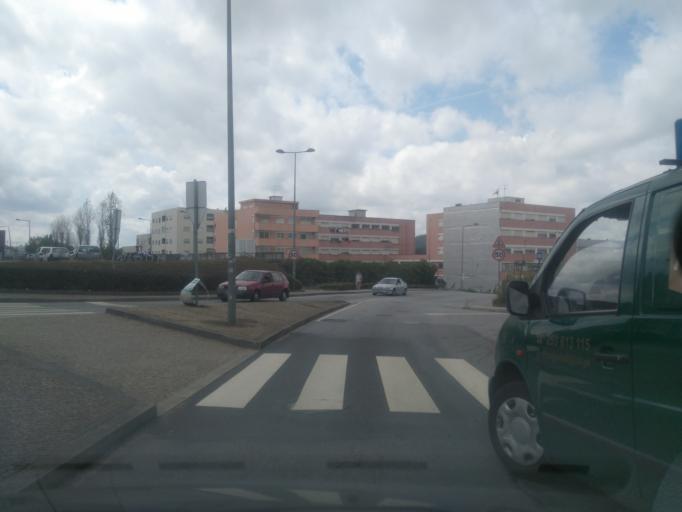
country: PT
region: Braga
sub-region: Braga
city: Braga
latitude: 41.5494
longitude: -8.4343
